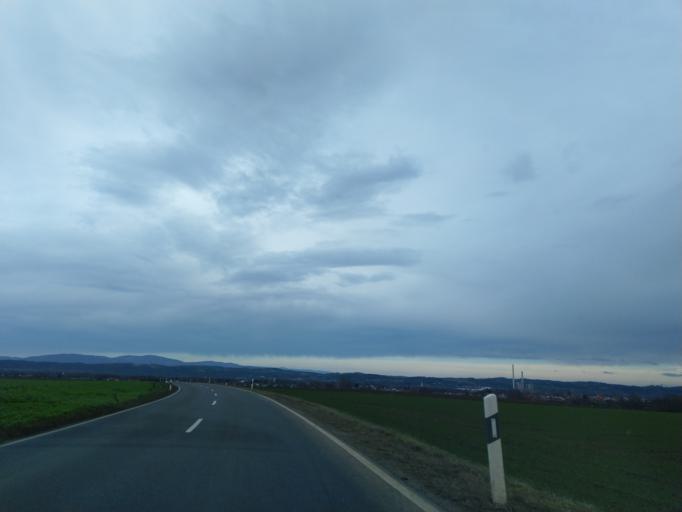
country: DE
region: Bavaria
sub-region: Lower Bavaria
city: Kunzing
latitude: 48.6579
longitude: 13.0619
